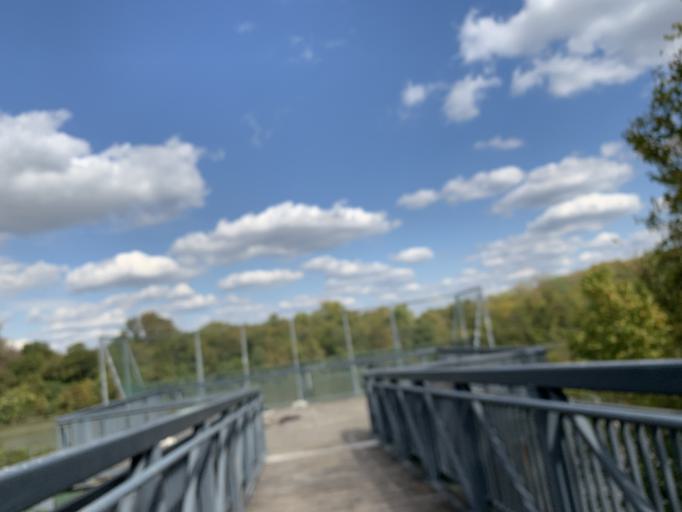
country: US
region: Kentucky
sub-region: Jefferson County
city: Louisville
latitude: 38.2668
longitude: -85.7757
